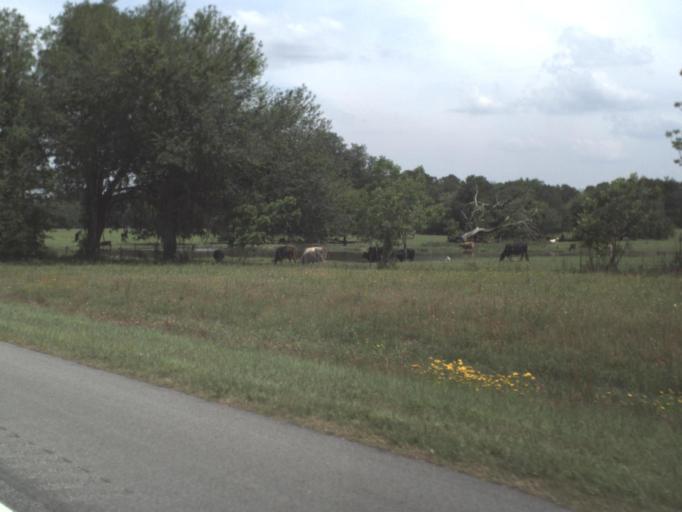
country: US
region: Florida
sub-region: Suwannee County
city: Live Oak
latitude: 30.3499
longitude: -83.0522
